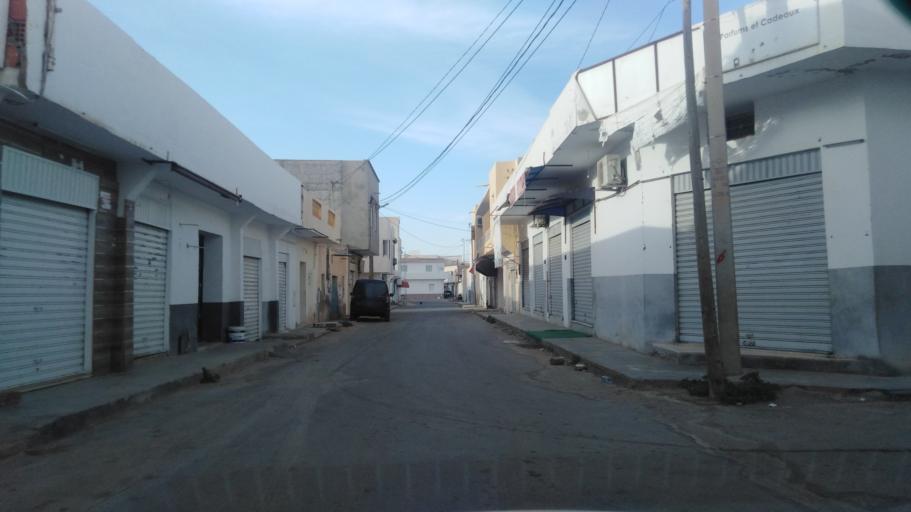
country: TN
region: Tataouine
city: Tataouine
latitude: 32.9362
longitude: 10.4533
